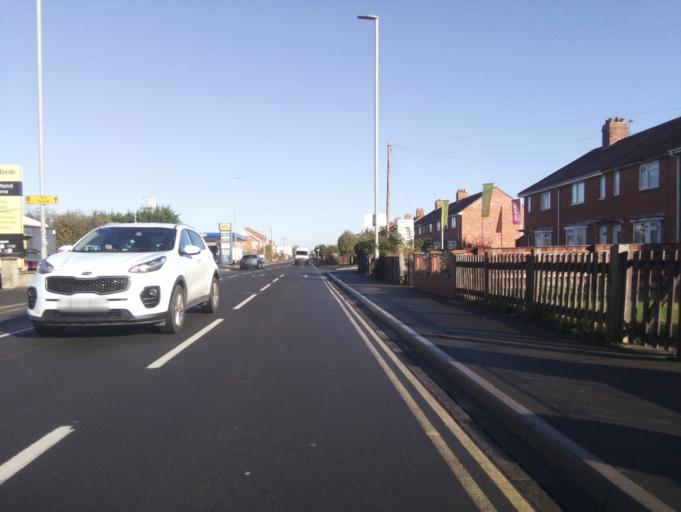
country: GB
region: England
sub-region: Somerset
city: Bridgwater
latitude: 51.1357
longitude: -2.9938
